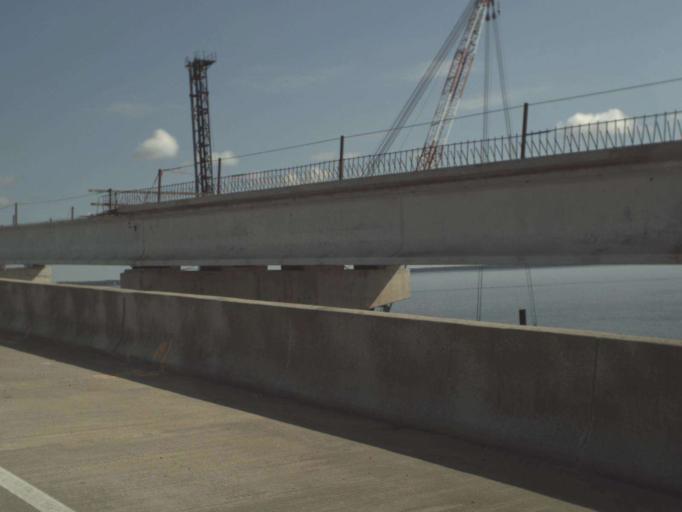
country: US
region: Florida
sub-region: Walton County
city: Seaside
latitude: 30.3976
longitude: -86.1700
